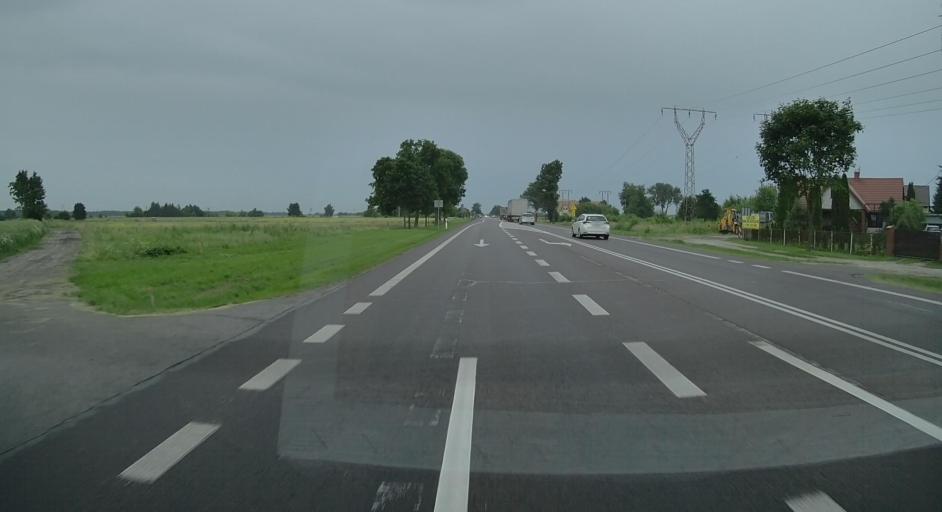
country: PL
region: Lublin Voivodeship
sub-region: Powiat bialski
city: Miedzyrzec Podlaski
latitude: 52.0002
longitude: 22.7783
